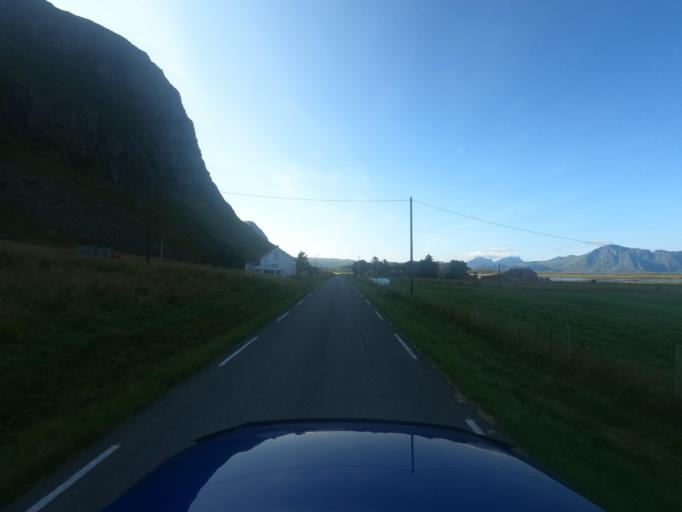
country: NO
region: Nordland
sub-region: Vestvagoy
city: Evjen
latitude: 68.3397
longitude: 13.9253
